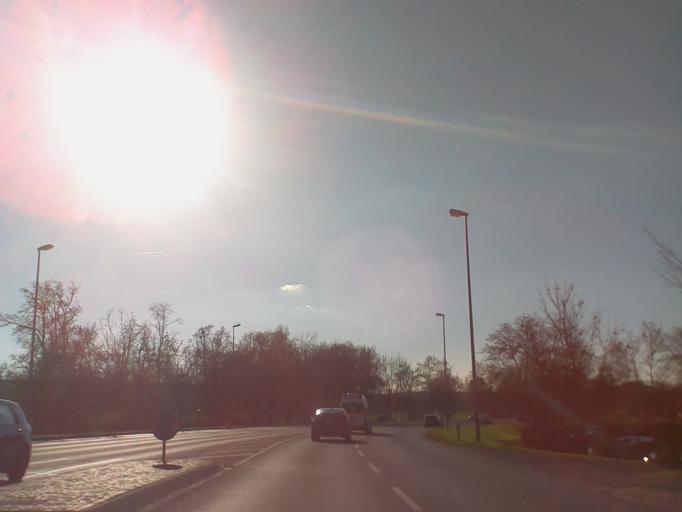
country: DE
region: Bavaria
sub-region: Regierungsbezirk Unterfranken
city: Bad Neustadt an der Saale
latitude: 50.3233
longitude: 10.2210
